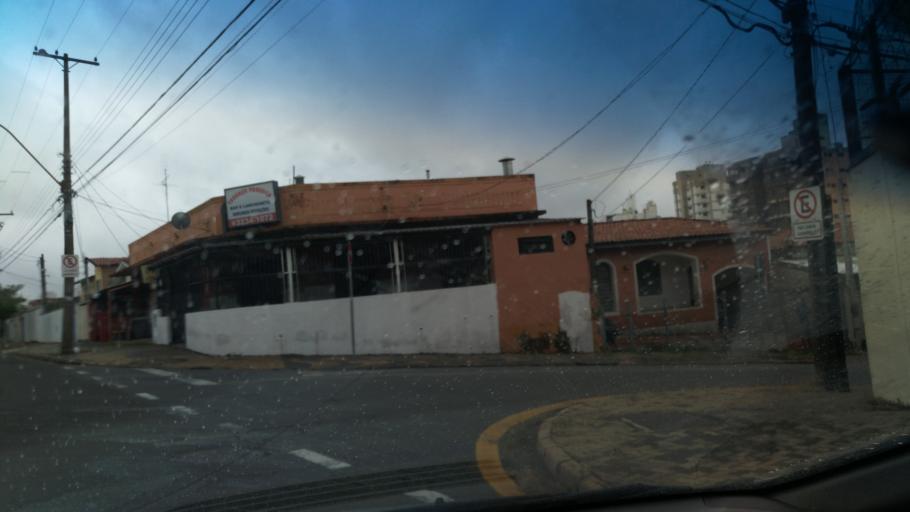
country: BR
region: Sao Paulo
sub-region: Campinas
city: Campinas
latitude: -22.9158
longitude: -47.0453
